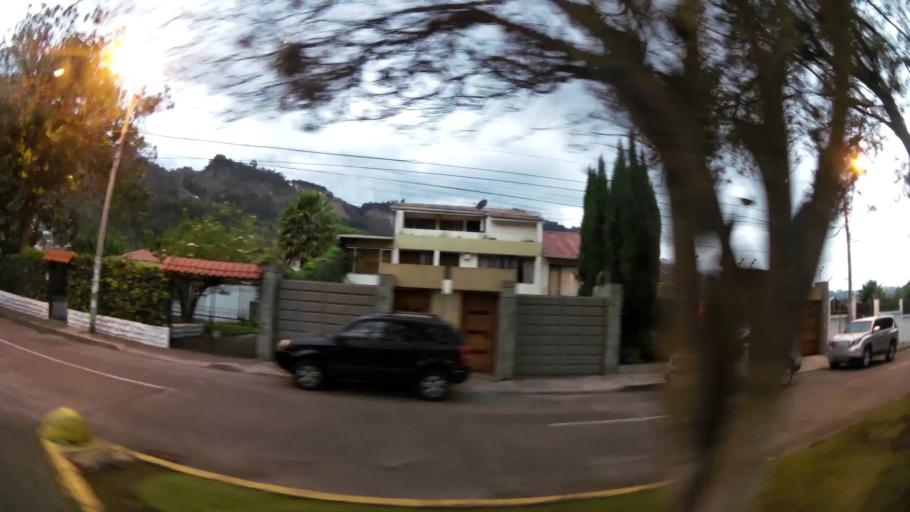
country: EC
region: Tungurahua
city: Ambato
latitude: -1.2545
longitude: -78.6441
